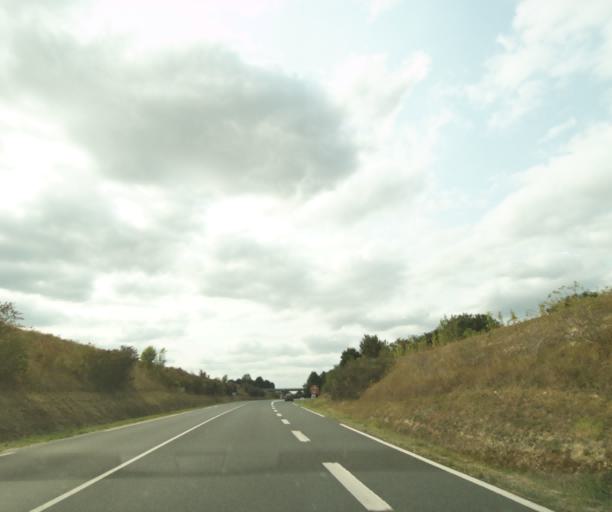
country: FR
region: Centre
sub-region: Departement de l'Indre
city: Buzancais
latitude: 46.8787
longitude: 1.4177
